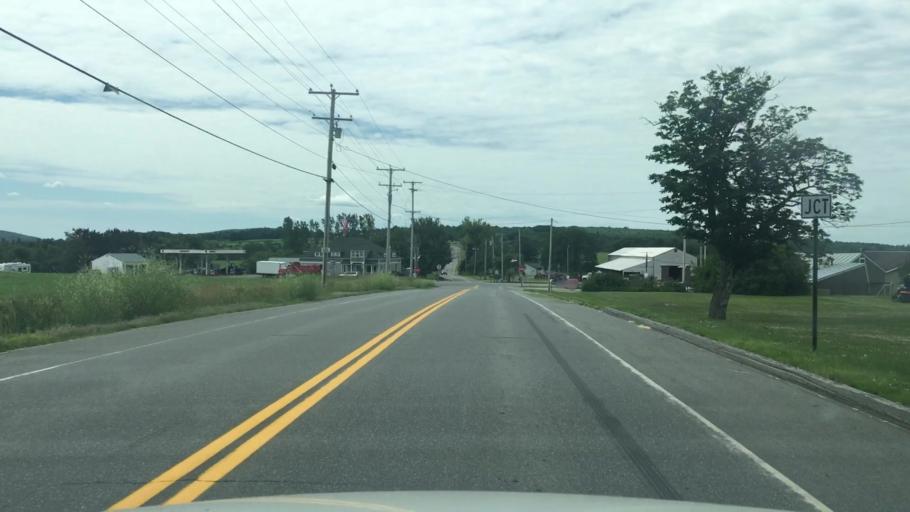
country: US
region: Maine
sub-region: Waldo County
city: Troy
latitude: 44.5339
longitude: -69.2700
